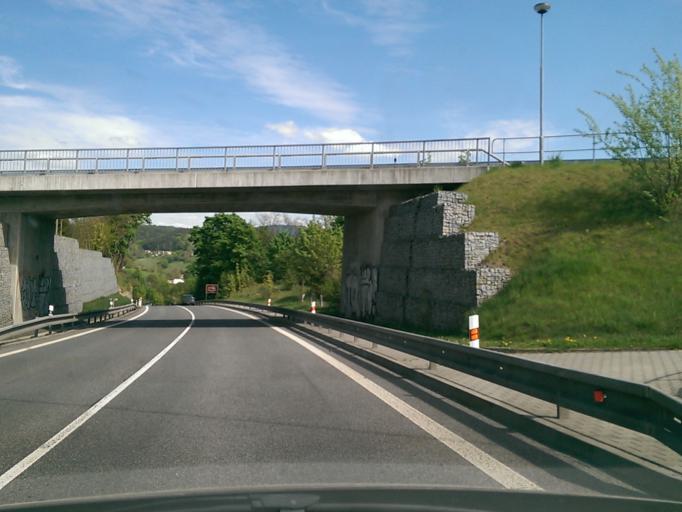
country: CZ
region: Liberecky
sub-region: Okres Semily
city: Turnov
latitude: 50.6033
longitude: 15.1630
